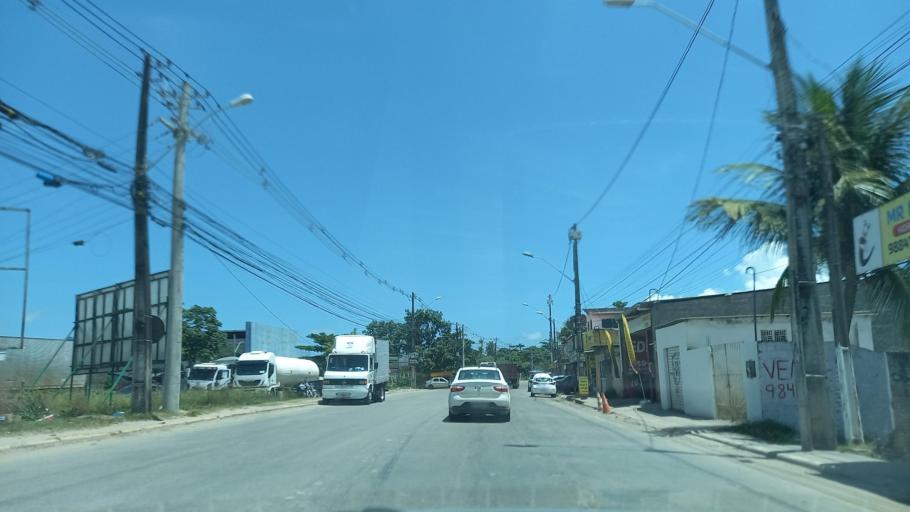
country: BR
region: Pernambuco
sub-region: Jaboatao Dos Guararapes
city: Jaboatao
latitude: -8.1540
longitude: -34.9589
